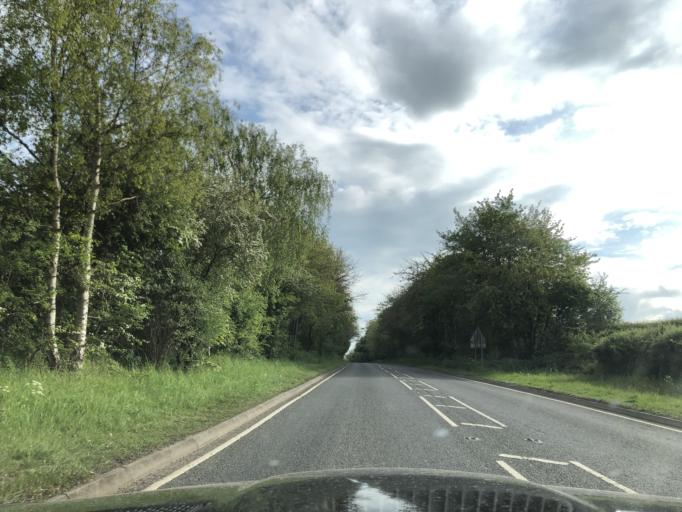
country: GB
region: England
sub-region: Warwickshire
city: Shipston on Stour
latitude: 52.1038
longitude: -1.6241
